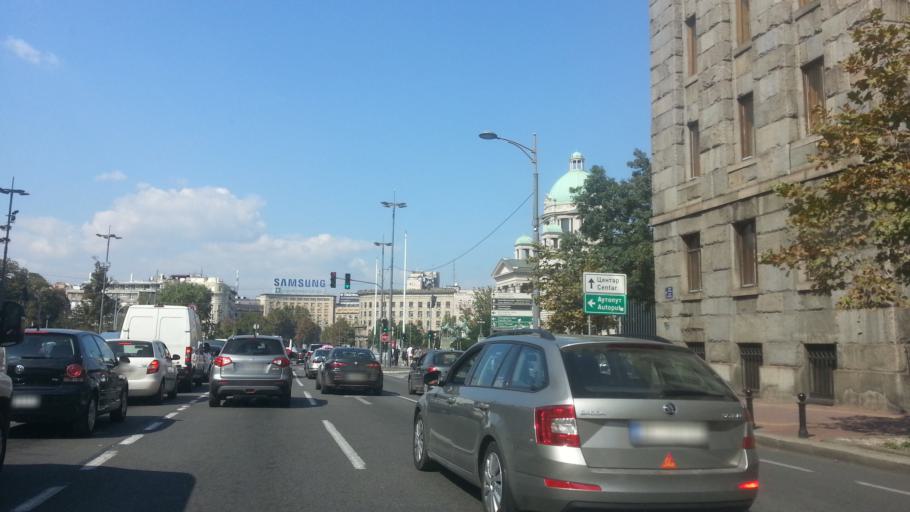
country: RS
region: Central Serbia
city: Belgrade
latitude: 44.8103
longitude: 20.4668
